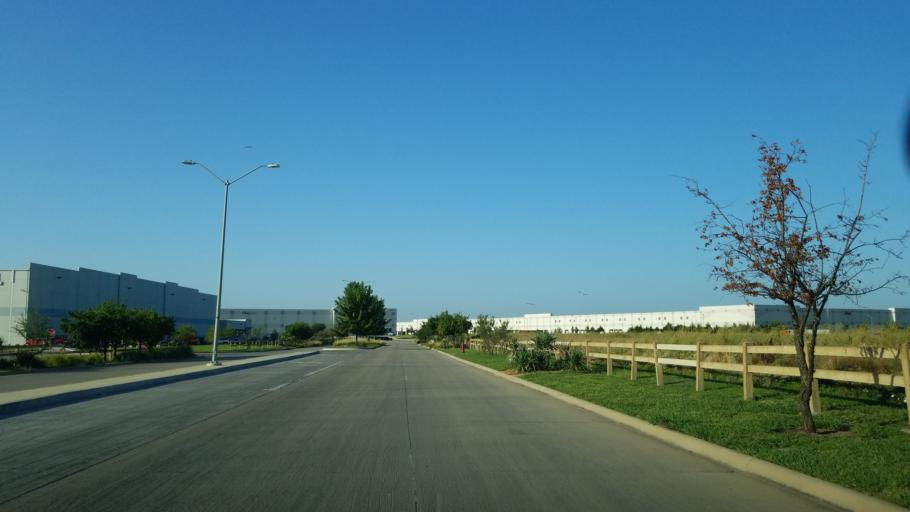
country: US
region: Texas
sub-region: Dallas County
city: Irving
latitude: 32.7615
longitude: -96.9471
